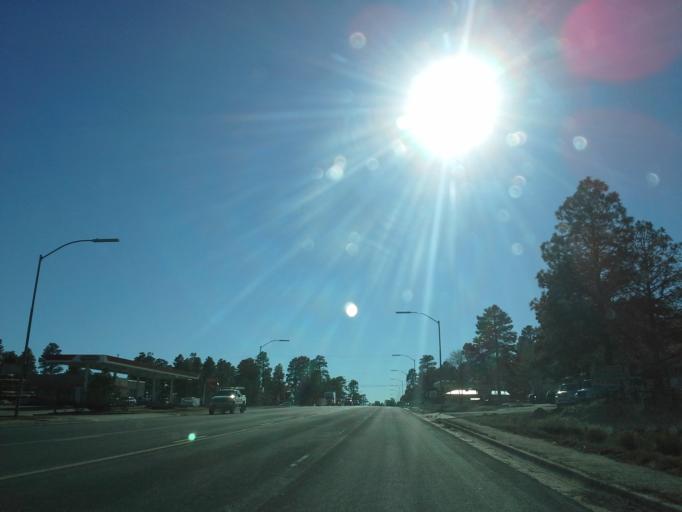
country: US
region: Arizona
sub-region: Coconino County
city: Flagstaff
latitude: 35.2433
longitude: -111.5671
